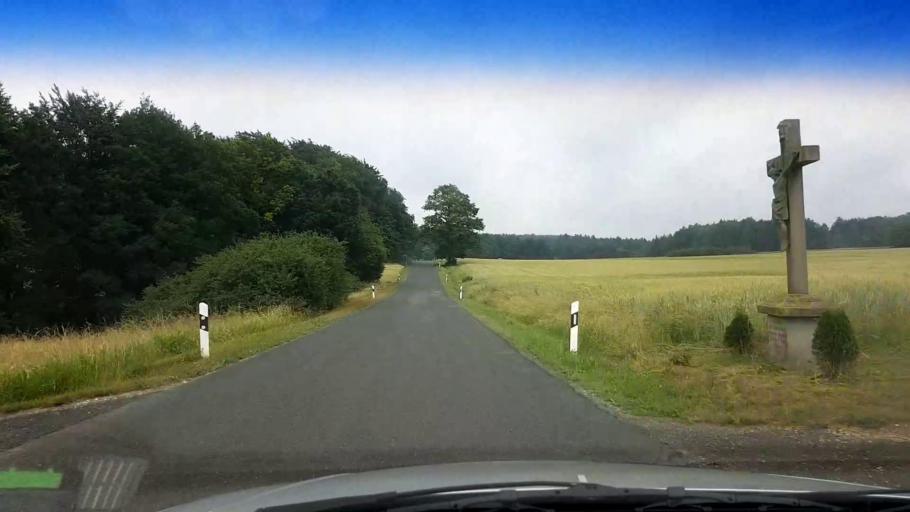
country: DE
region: Bavaria
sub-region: Upper Franconia
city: Wattendorf
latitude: 50.0601
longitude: 11.1014
